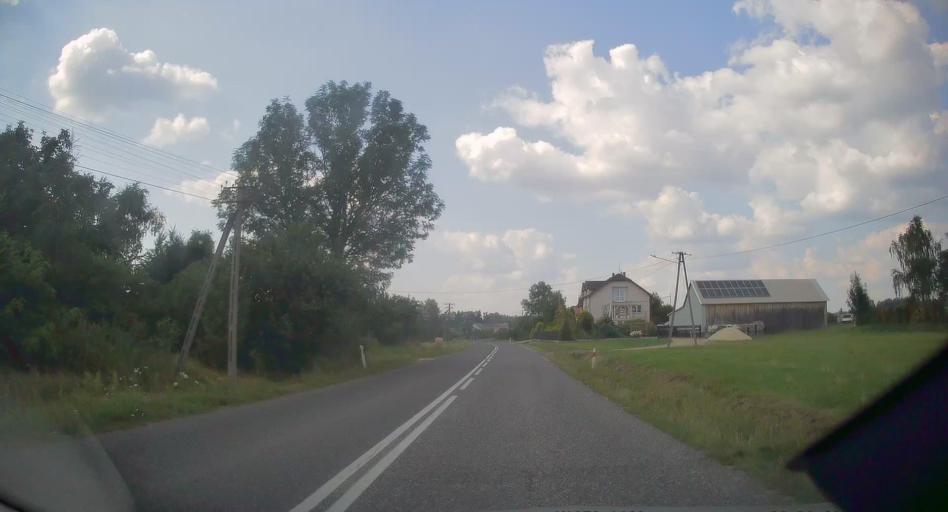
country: PL
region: Swietokrzyskie
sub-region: Powiat kielecki
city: Lopuszno
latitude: 50.9071
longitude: 20.2465
